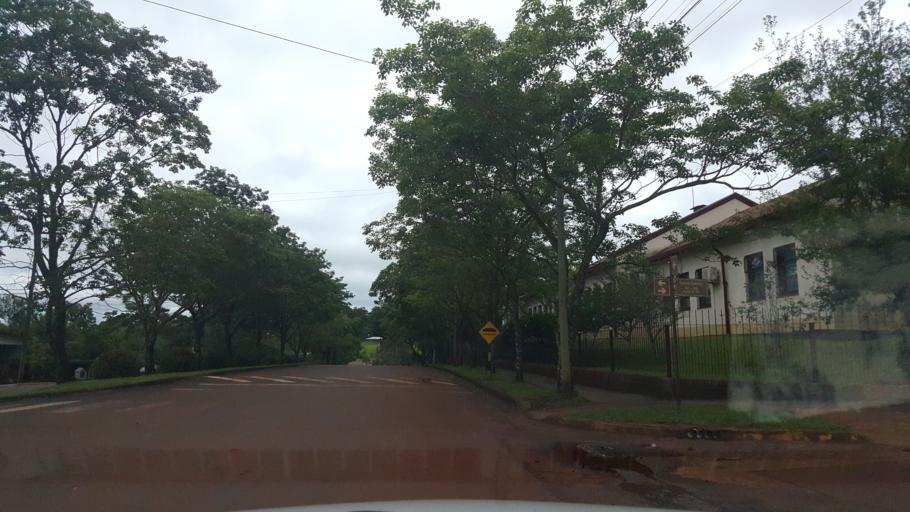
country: AR
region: Misiones
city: Ruiz de Montoya
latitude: -26.9854
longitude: -55.0492
